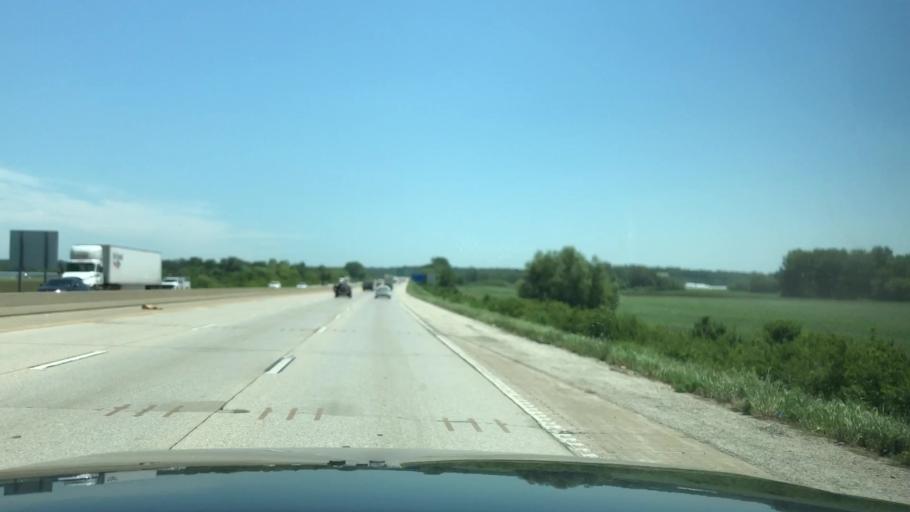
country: US
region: Missouri
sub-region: Saint Charles County
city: Saint Charles
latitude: 38.7914
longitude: -90.4429
